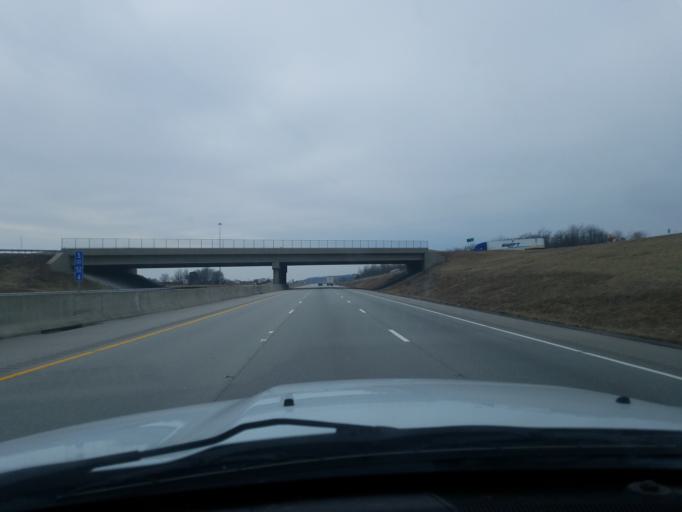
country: US
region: Kentucky
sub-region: Barren County
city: Cave City
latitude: 37.1362
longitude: -85.9770
